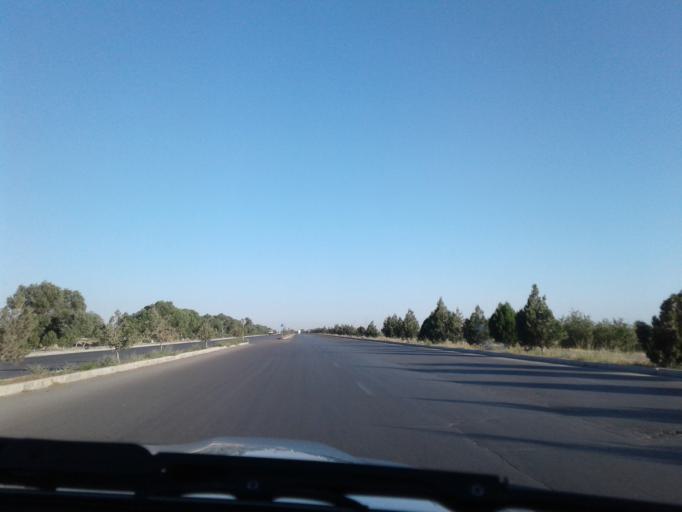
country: TM
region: Ahal
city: Abadan
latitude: 38.0661
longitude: 58.2537
